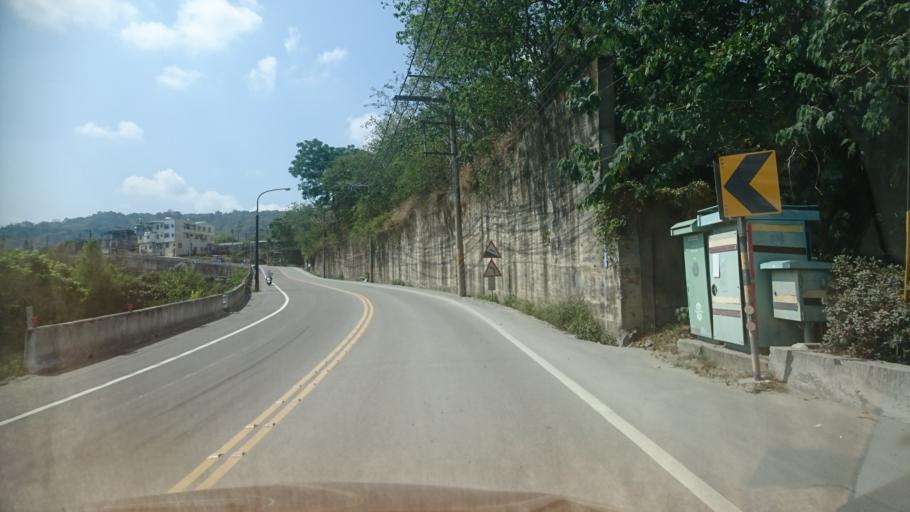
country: TW
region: Taiwan
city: Fengyuan
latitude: 24.2783
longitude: 120.7775
